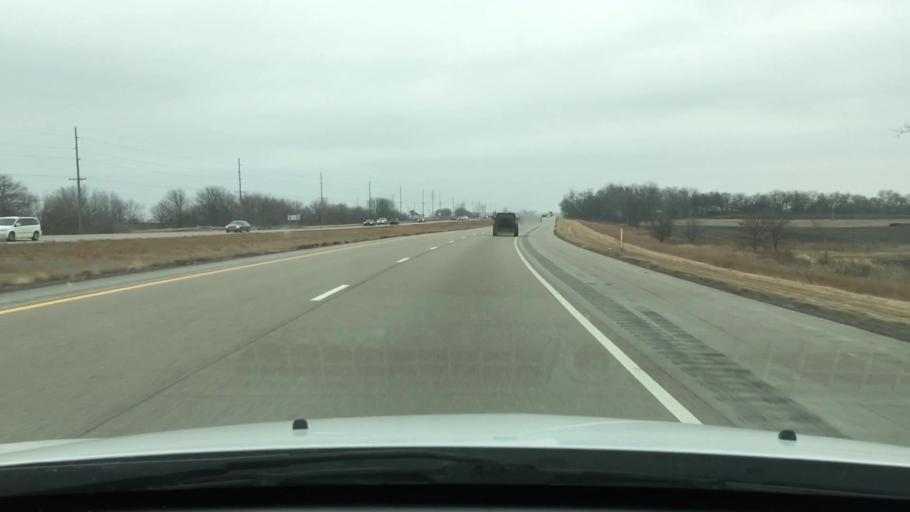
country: US
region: Illinois
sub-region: Logan County
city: Atlanta
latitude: 40.2789
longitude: -89.2099
